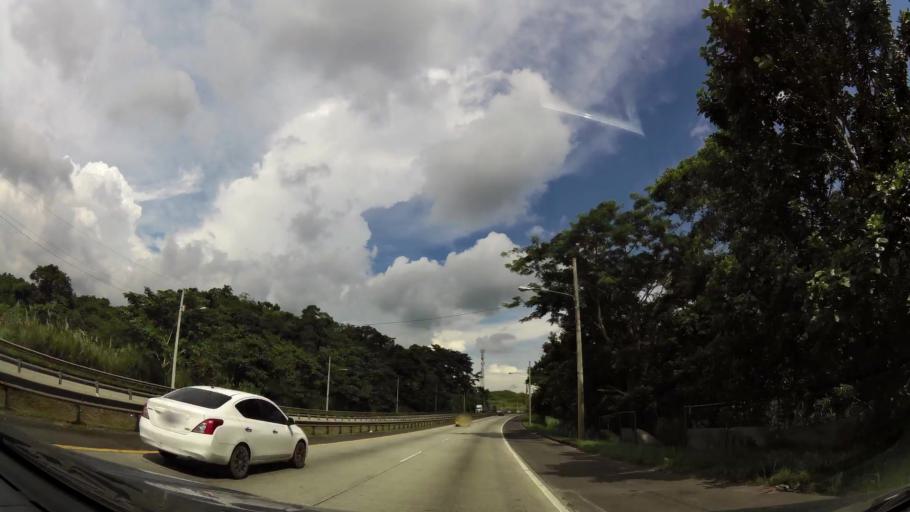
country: PA
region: Panama
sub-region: Distrito de Panama
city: Paraiso
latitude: 9.0406
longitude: -79.5689
